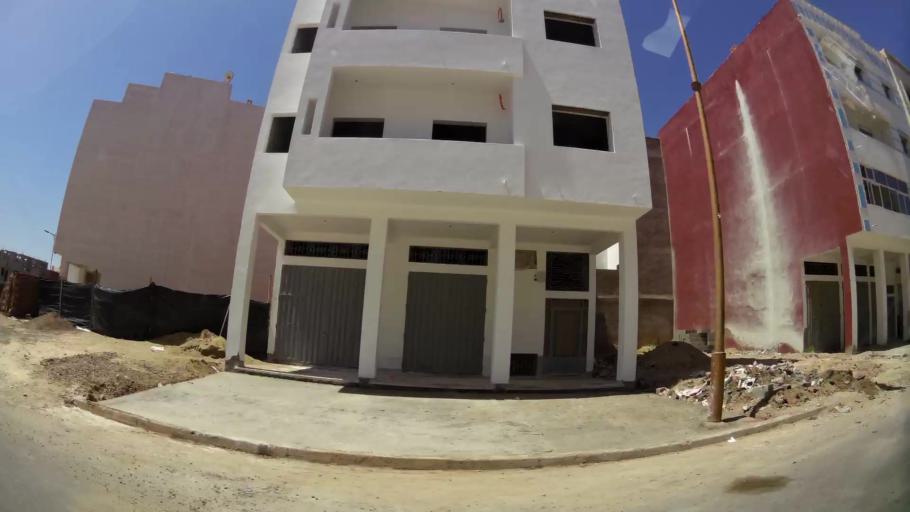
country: MA
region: Oued ed Dahab-Lagouira
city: Dakhla
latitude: 30.4301
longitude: -9.5525
